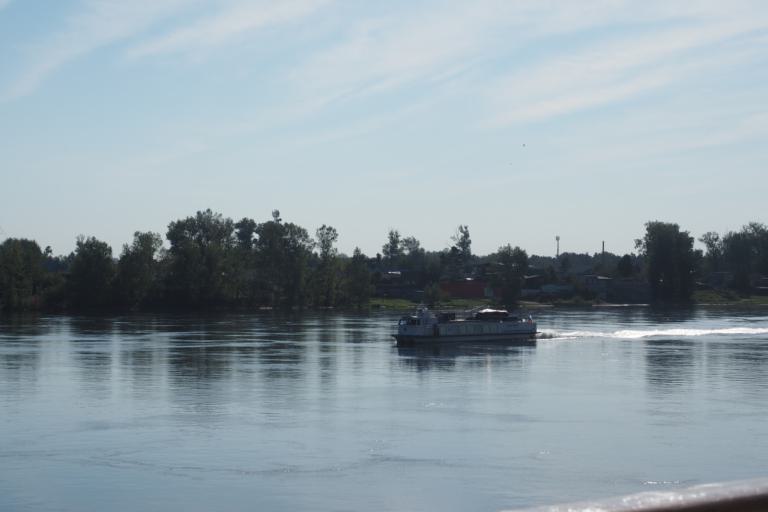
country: RU
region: Krasnoyarskiy
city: Berezovka
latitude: 56.1392
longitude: 93.1332
